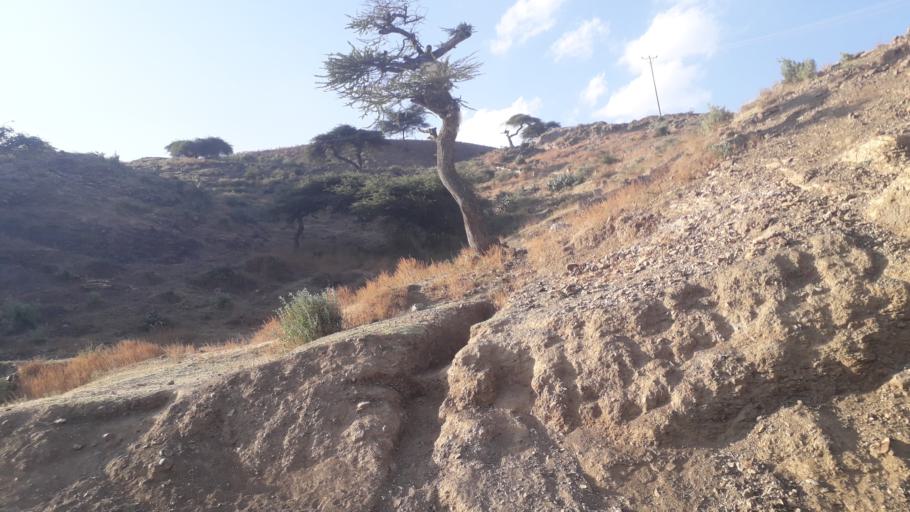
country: ET
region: Amhara
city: Dese
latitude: 11.5197
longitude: 39.2497
